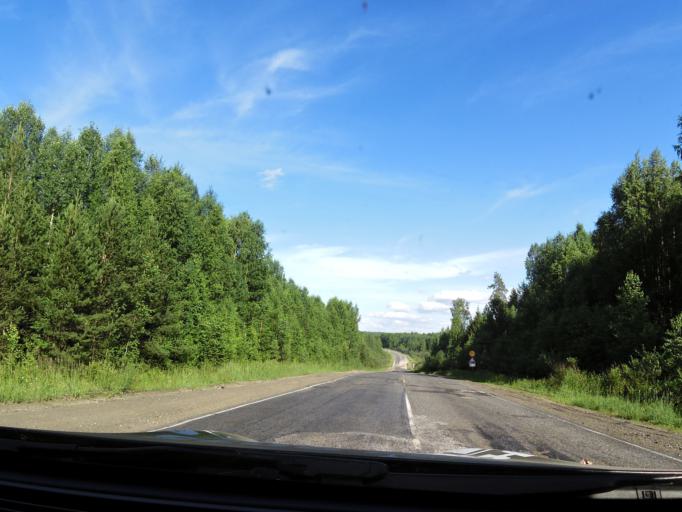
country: RU
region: Kirov
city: Dubrovka
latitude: 58.8938
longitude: 51.3333
